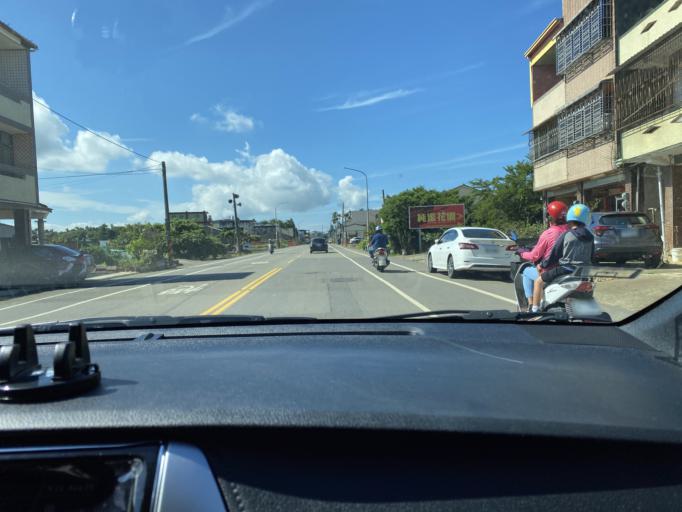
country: TW
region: Taiwan
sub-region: Nantou
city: Nantou
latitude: 23.9185
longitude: 120.6375
